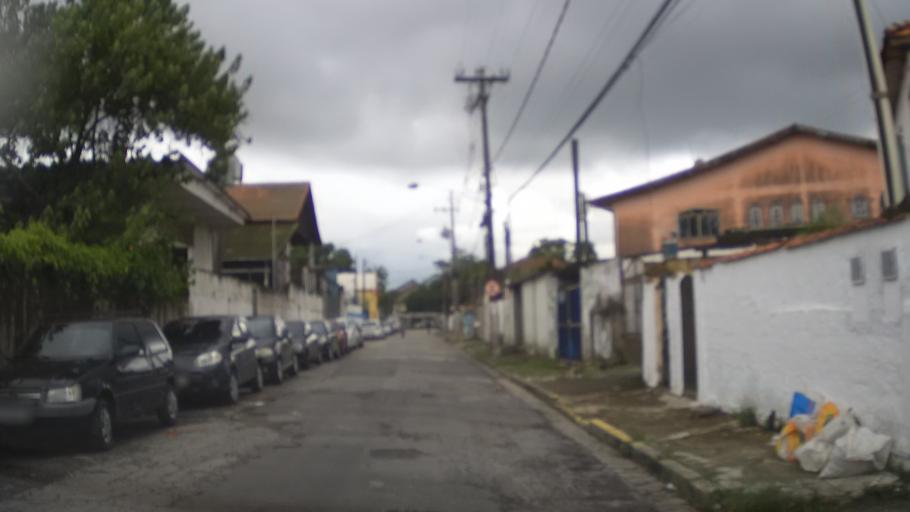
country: BR
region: Sao Paulo
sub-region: Santos
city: Santos
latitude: -23.9386
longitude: -46.3077
